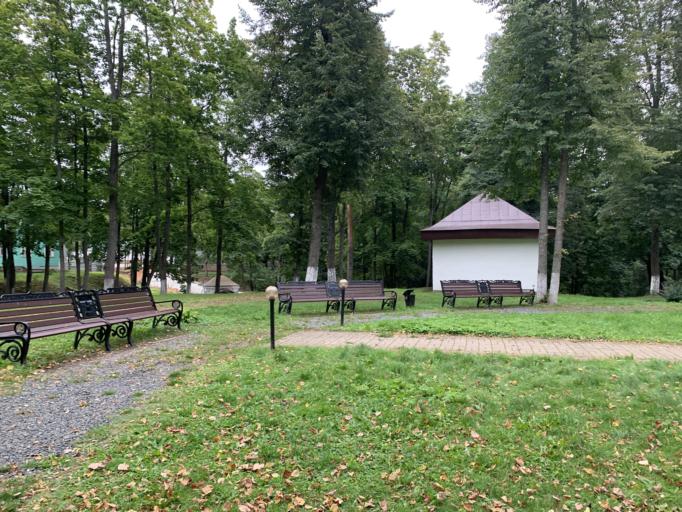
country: RU
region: Moskovskaya
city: Zvenigorod
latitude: 55.7297
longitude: 36.8158
